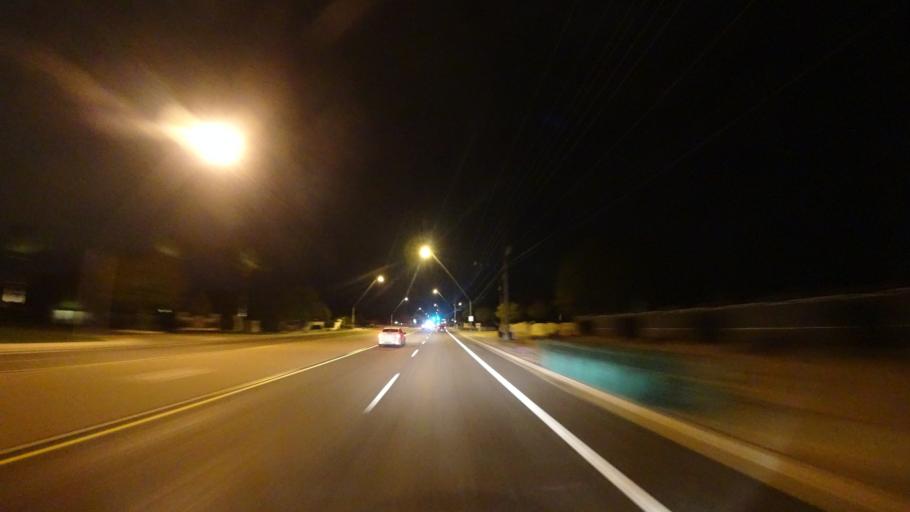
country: US
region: Arizona
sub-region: Maricopa County
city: Mesa
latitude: 33.4561
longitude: -111.7533
